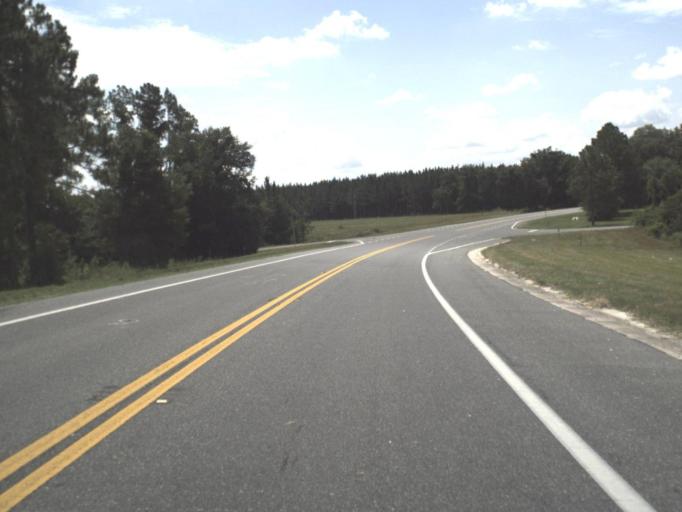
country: US
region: Florida
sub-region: Suwannee County
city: Live Oak
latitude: 30.1545
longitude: -82.9515
